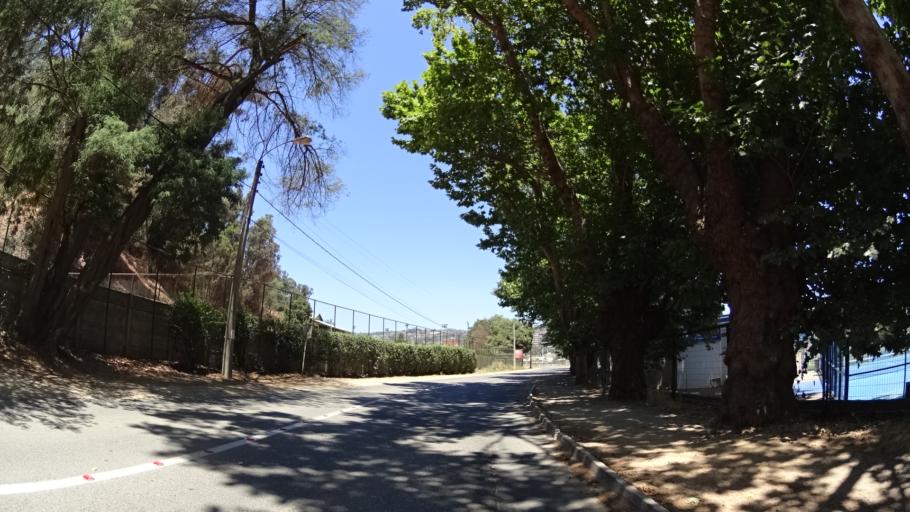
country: CL
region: Valparaiso
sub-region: Provincia de Valparaiso
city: Vina del Mar
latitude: -33.0217
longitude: -71.5351
